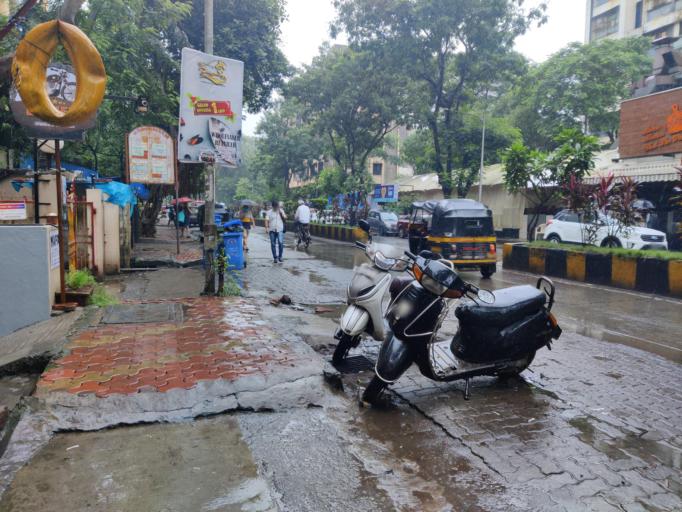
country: IN
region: Maharashtra
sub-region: Mumbai Suburban
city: Borivli
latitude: 19.2430
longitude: 72.8656
